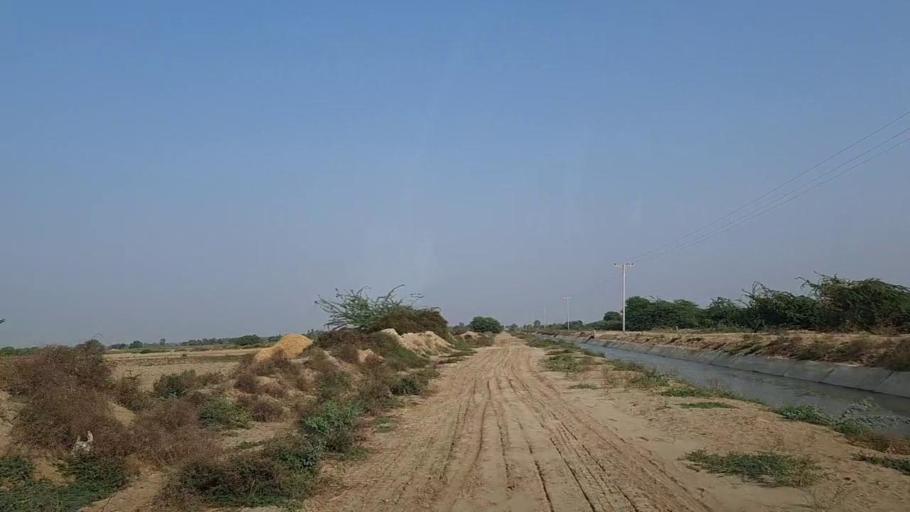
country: PK
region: Sindh
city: Mirpur Sakro
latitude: 24.6155
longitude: 67.7241
